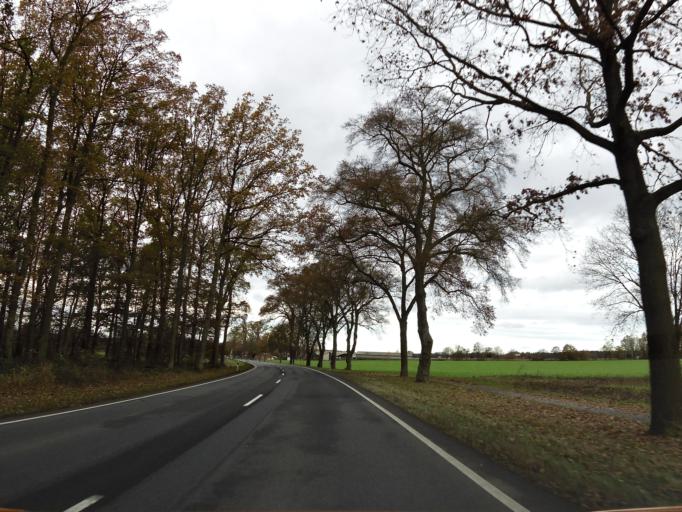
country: DE
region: Lower Saxony
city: Suderburg
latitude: 52.9533
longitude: 10.4928
